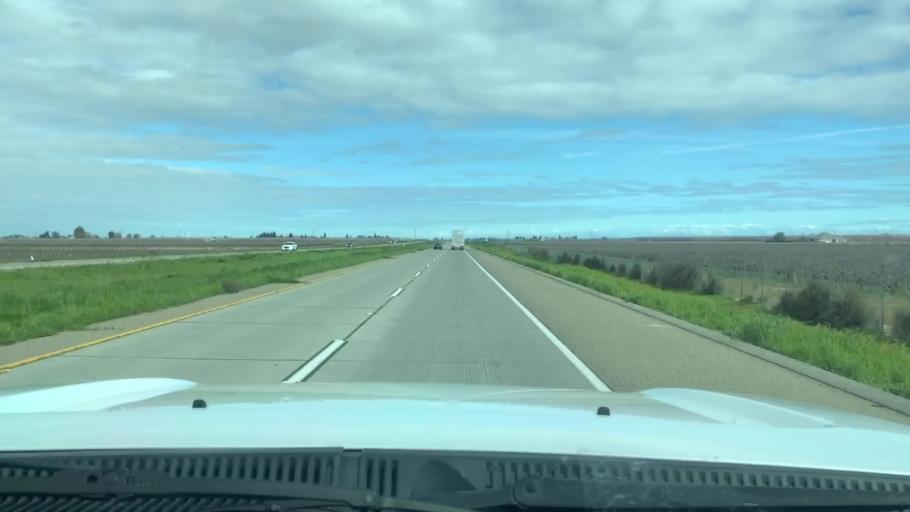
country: US
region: California
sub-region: Fresno County
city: Caruthers
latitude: 36.5699
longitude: -119.7859
